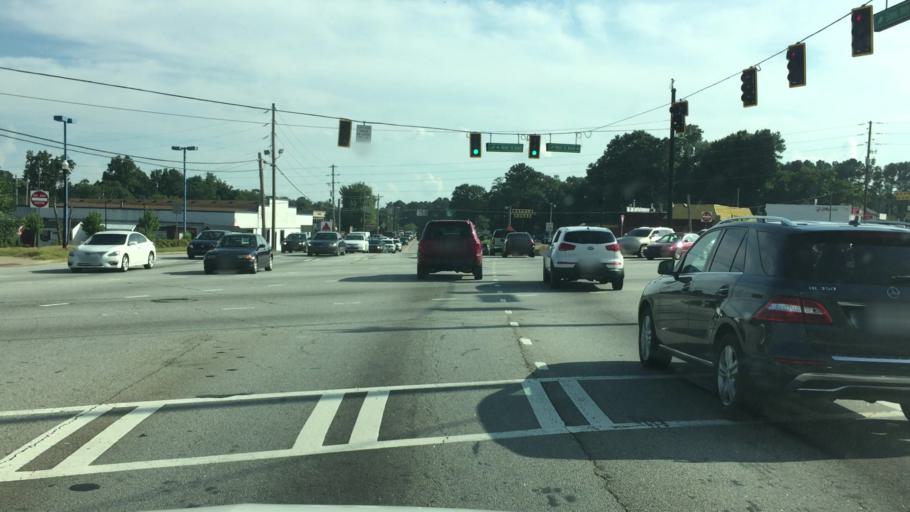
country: US
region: Georgia
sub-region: Gwinnett County
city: Snellville
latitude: 33.8578
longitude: -84.0200
